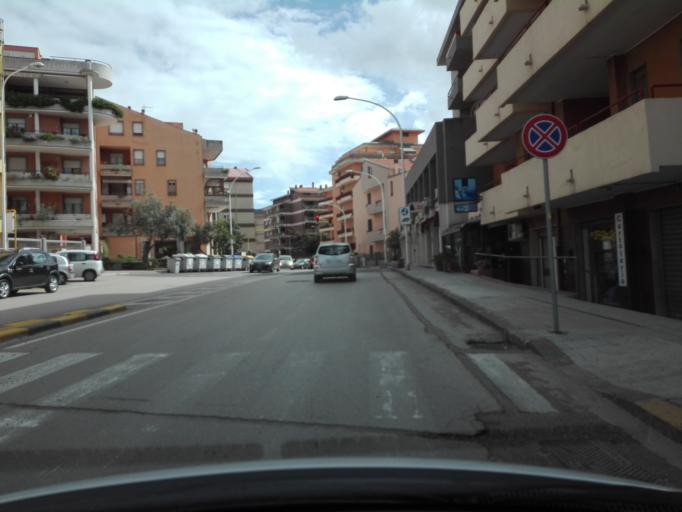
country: IT
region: Sardinia
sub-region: Provincia di Sassari
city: Sassari
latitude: 40.7284
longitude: 8.5754
